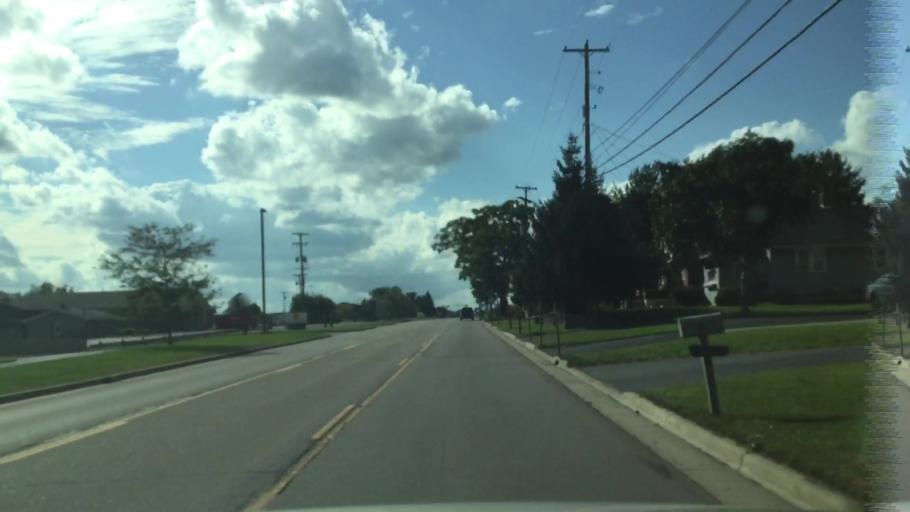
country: US
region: Michigan
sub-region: Shiawassee County
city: Owosso
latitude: 42.9976
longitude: -84.1995
